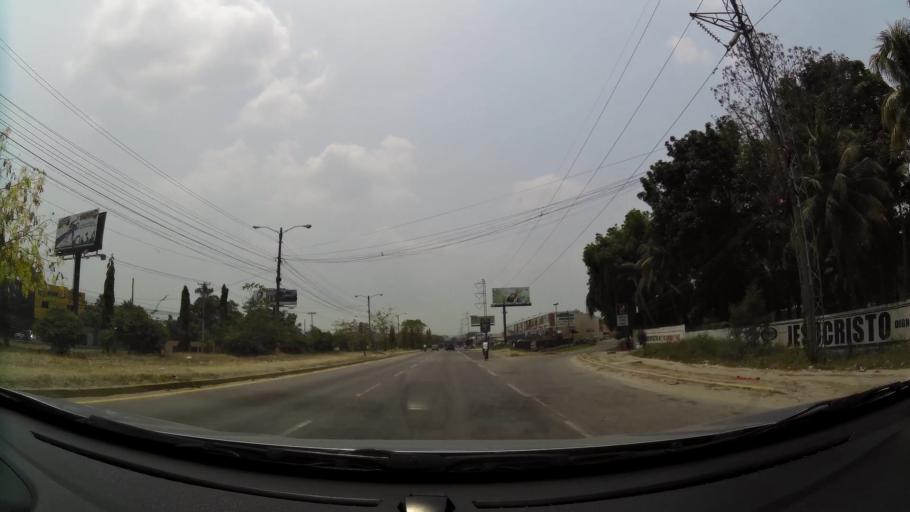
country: HN
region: Cortes
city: San Pedro Sula
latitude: 15.4798
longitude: -87.9757
